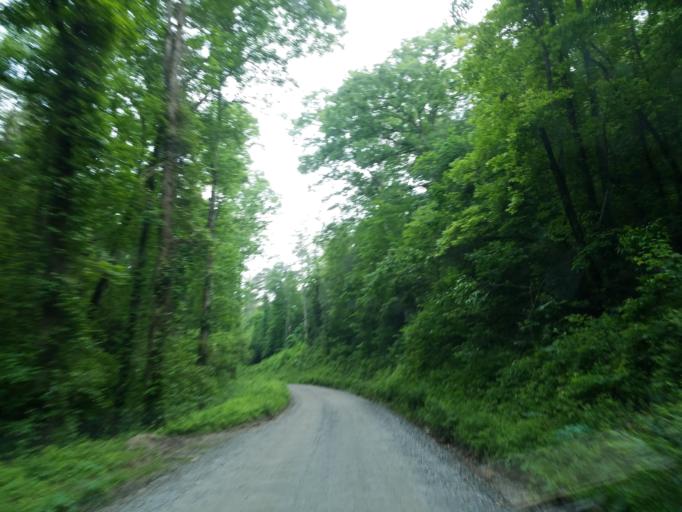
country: US
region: Georgia
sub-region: Dawson County
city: Dawsonville
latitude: 34.5674
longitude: -84.1363
